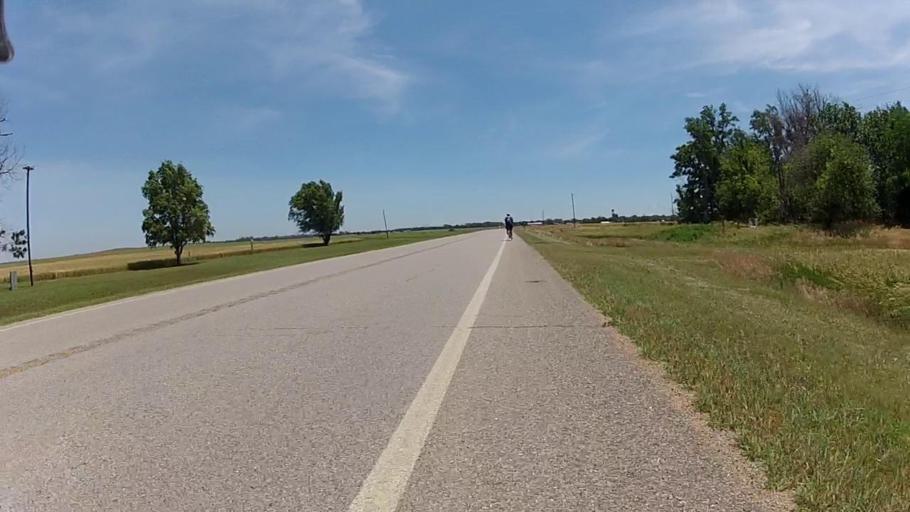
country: US
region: Kansas
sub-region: Barber County
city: Medicine Lodge
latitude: 37.2534
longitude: -98.4325
